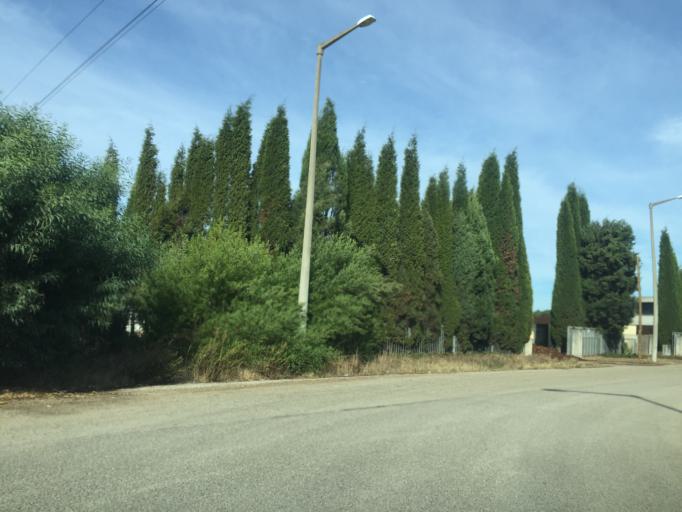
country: PT
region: Coimbra
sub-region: Figueira da Foz
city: Lavos
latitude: 40.1072
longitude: -8.8516
